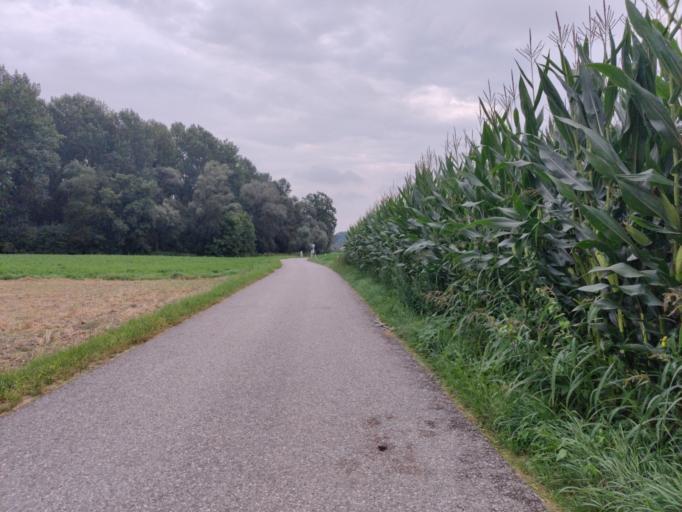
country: AT
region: Upper Austria
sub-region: Politischer Bezirk Linz-Land
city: Asten
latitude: 48.2328
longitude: 14.4454
